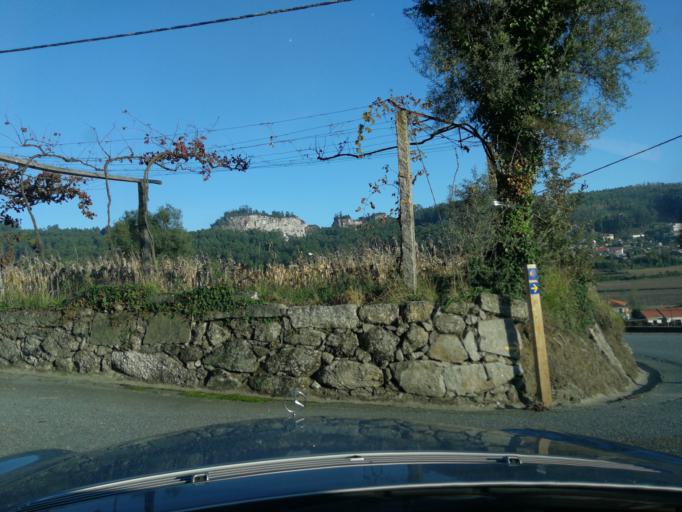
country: PT
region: Braga
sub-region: Braga
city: Oliveira
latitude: 41.4597
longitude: -8.4502
